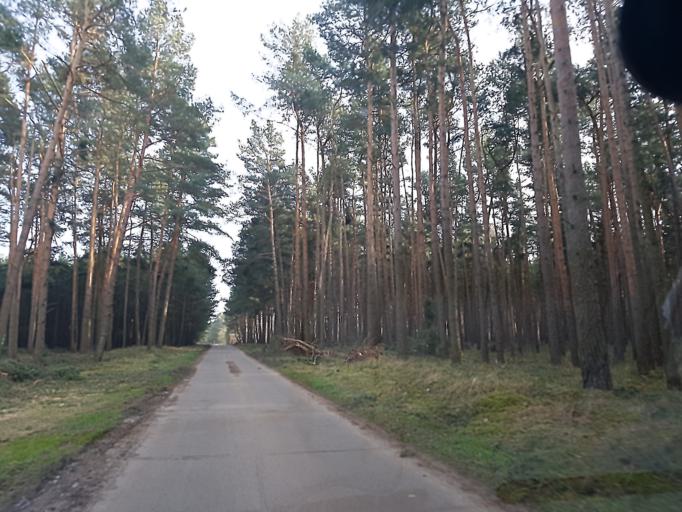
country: DE
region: Brandenburg
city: Wollin
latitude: 52.2715
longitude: 12.4888
